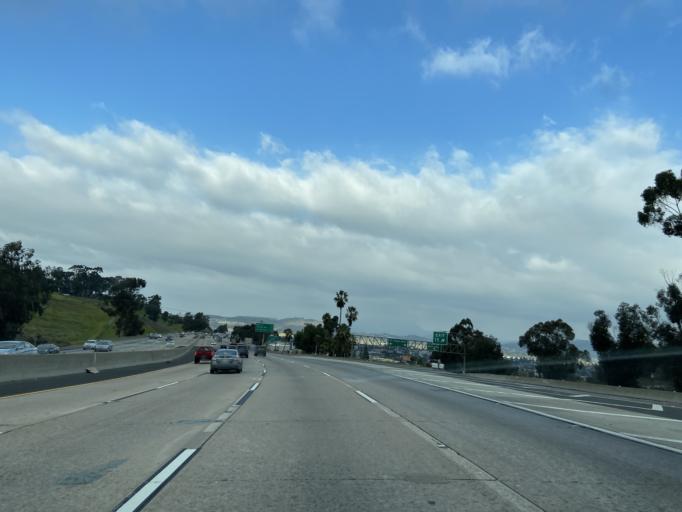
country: US
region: California
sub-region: San Diego County
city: Casa de Oro-Mount Helix
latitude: 32.7806
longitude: -116.9823
